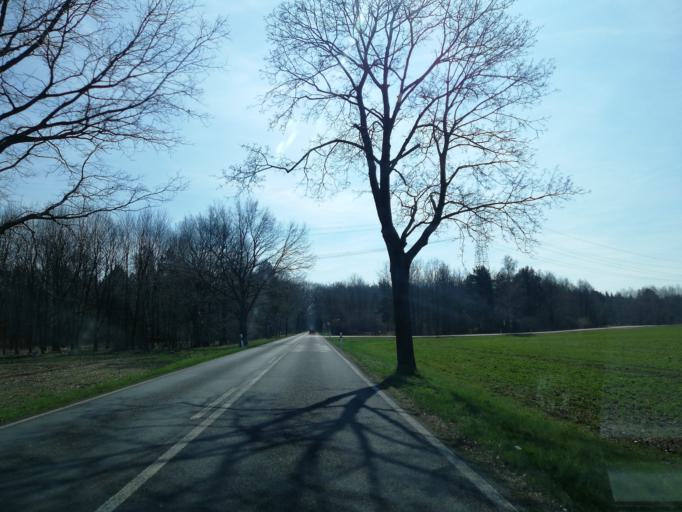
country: DE
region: Brandenburg
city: Altdobern
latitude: 51.6625
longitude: 14.0369
